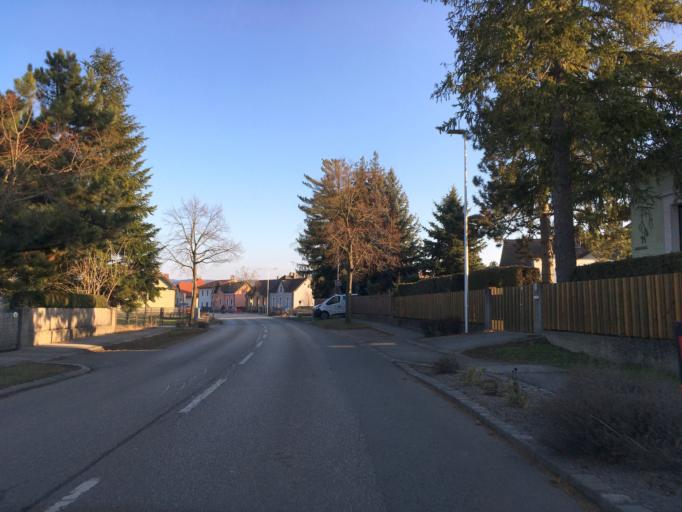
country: AT
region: Lower Austria
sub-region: Politischer Bezirk Tulln
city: Konigstetten
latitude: 48.3316
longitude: 16.1567
